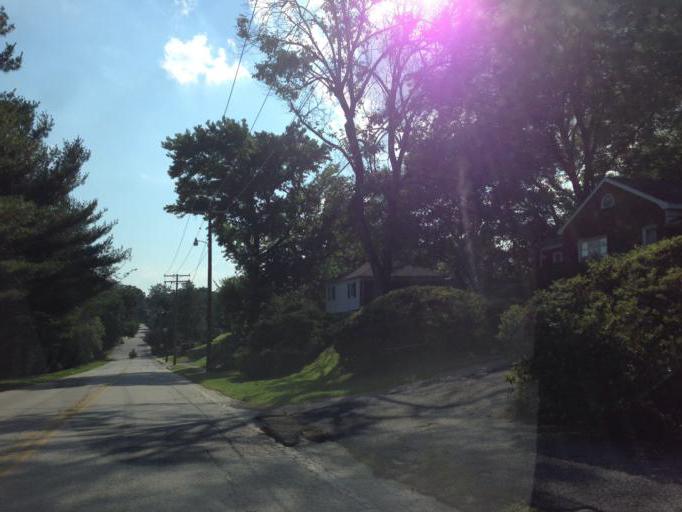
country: US
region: Maryland
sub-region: Baltimore County
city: Towson
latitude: 39.3862
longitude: -76.5928
